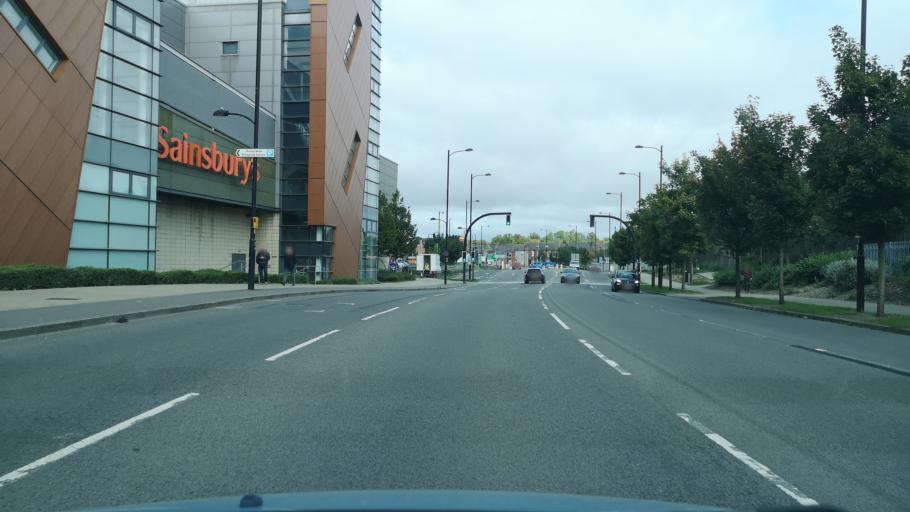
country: GB
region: England
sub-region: City and Borough of Wakefield
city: Wakefield
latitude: 53.6843
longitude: -1.4927
